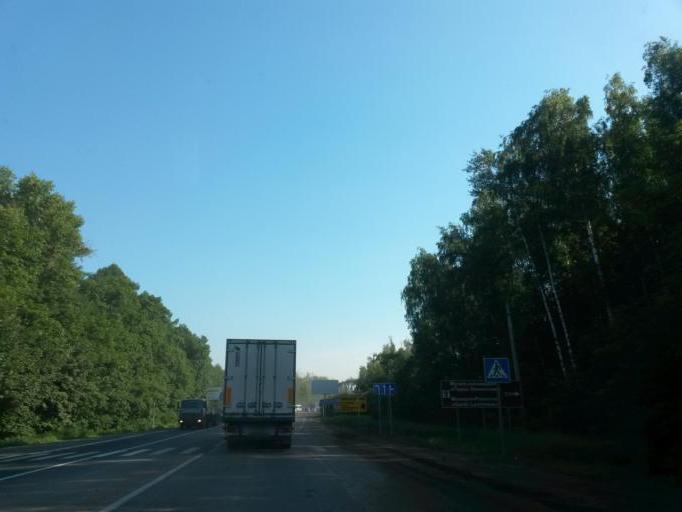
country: RU
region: Moskovskaya
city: Gorki-Leninskiye
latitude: 55.5302
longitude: 37.7676
